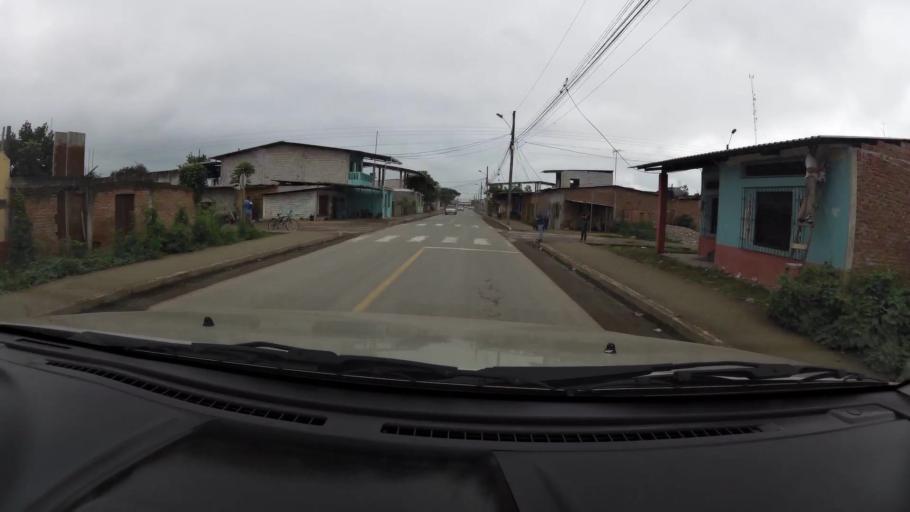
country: EC
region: El Oro
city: Pasaje
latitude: -3.3381
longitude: -79.8119
